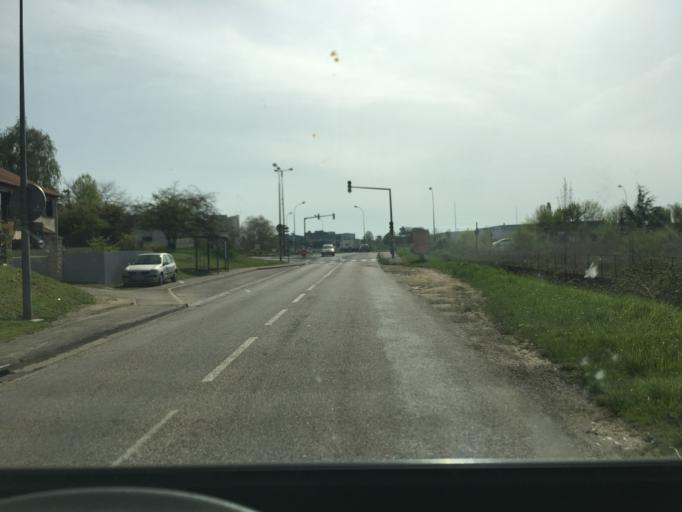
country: FR
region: Lorraine
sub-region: Departement de Meurthe-et-Moselle
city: Chaligny
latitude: 48.6173
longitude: 6.0897
